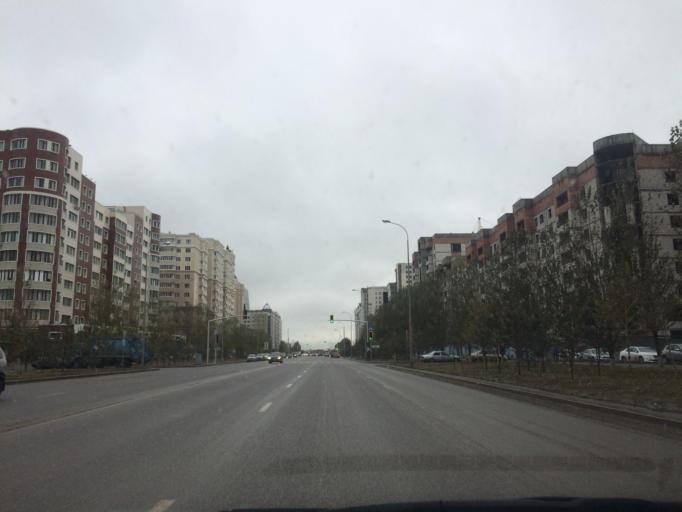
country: KZ
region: Astana Qalasy
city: Astana
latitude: 51.1137
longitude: 71.4285
